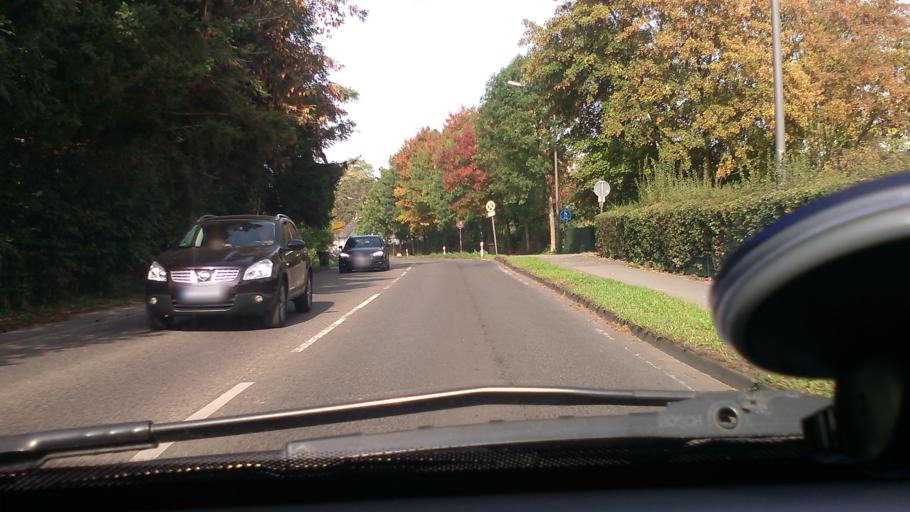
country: DE
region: North Rhine-Westphalia
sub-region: Regierungsbezirk Dusseldorf
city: Hilden
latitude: 51.1398
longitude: 6.9431
